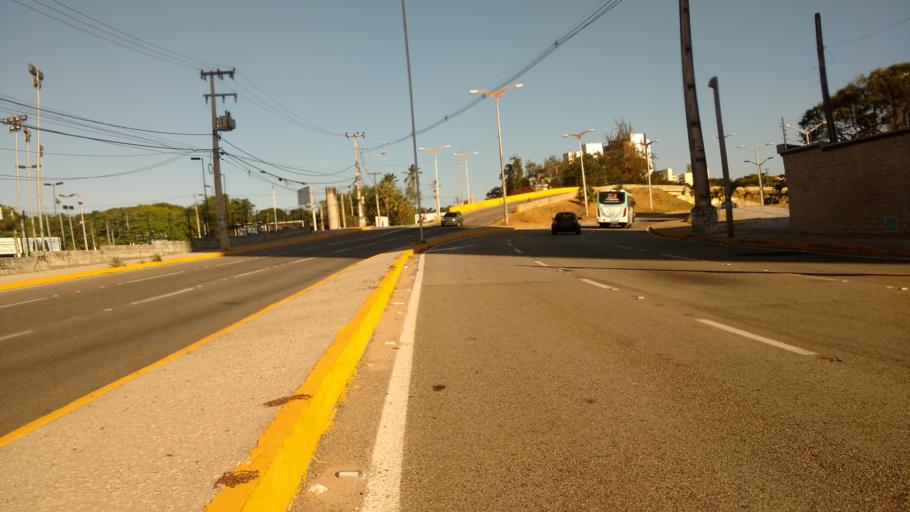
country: BR
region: Ceara
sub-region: Fortaleza
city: Fortaleza
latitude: -3.7586
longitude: -38.4845
